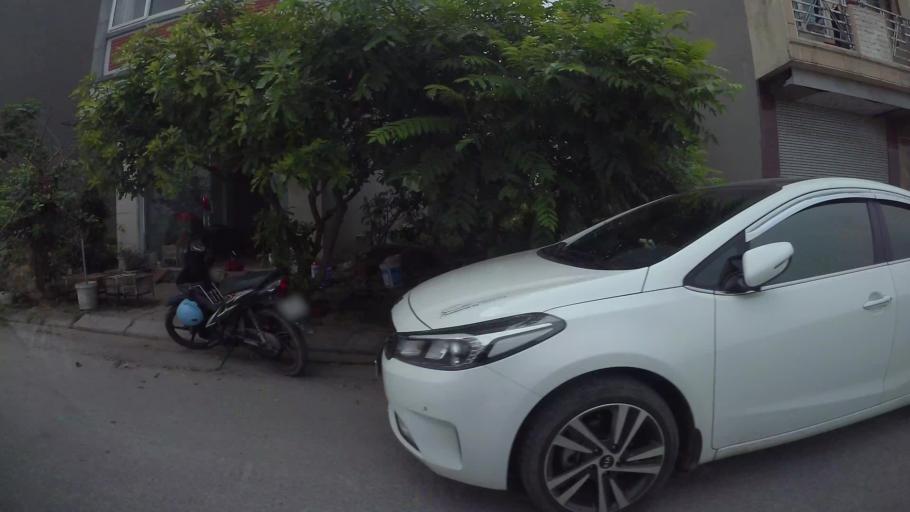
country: VN
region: Ha Noi
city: Trau Quy
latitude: 21.0657
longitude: 105.9154
